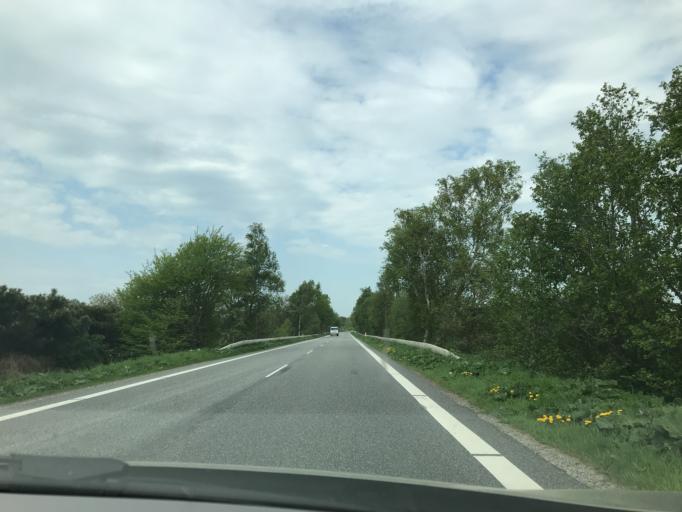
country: DK
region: South Denmark
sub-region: Assens Kommune
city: Assens
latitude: 55.3187
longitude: 9.9385
